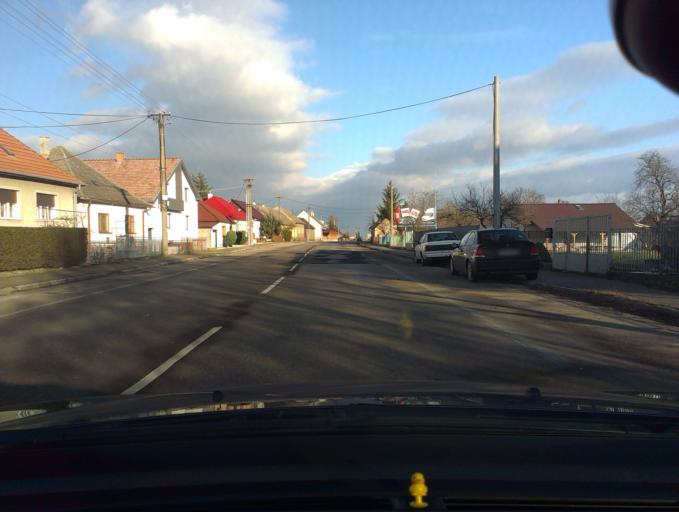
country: SK
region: Trnavsky
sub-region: Okres Trnava
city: Piestany
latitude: 48.6567
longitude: 17.8411
